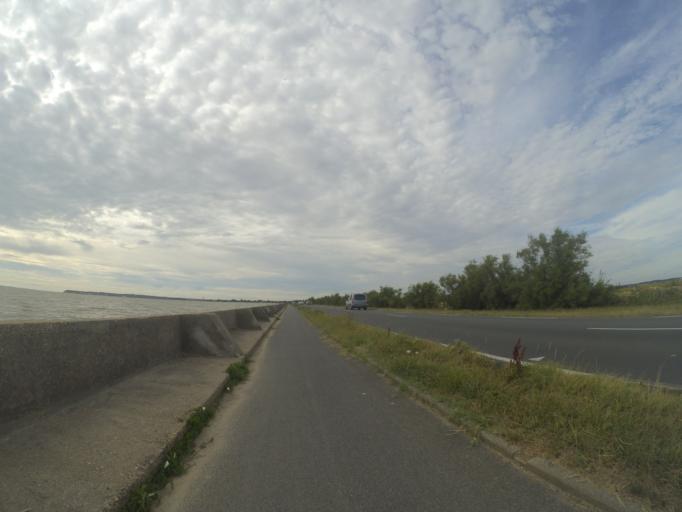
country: FR
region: Poitou-Charentes
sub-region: Departement de la Charente-Maritime
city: Meschers-sur-Gironde
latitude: 45.5420
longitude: -0.9085
